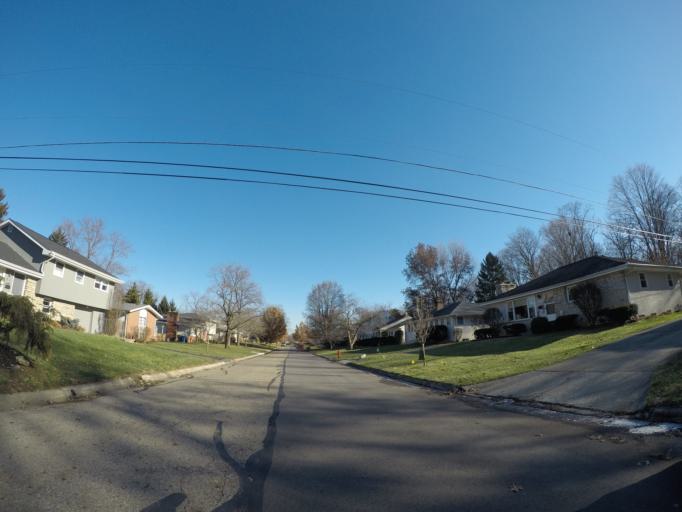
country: US
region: Ohio
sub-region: Franklin County
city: Upper Arlington
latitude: 40.0196
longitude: -83.0450
